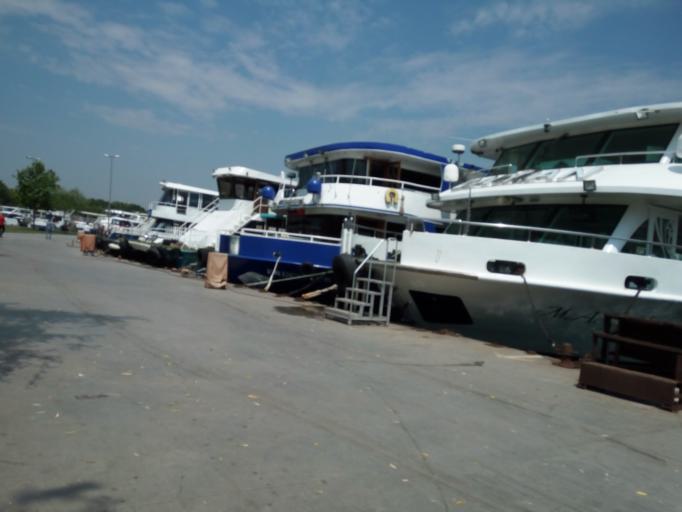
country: TR
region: Istanbul
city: Eminoenue
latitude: 41.0194
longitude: 28.9682
